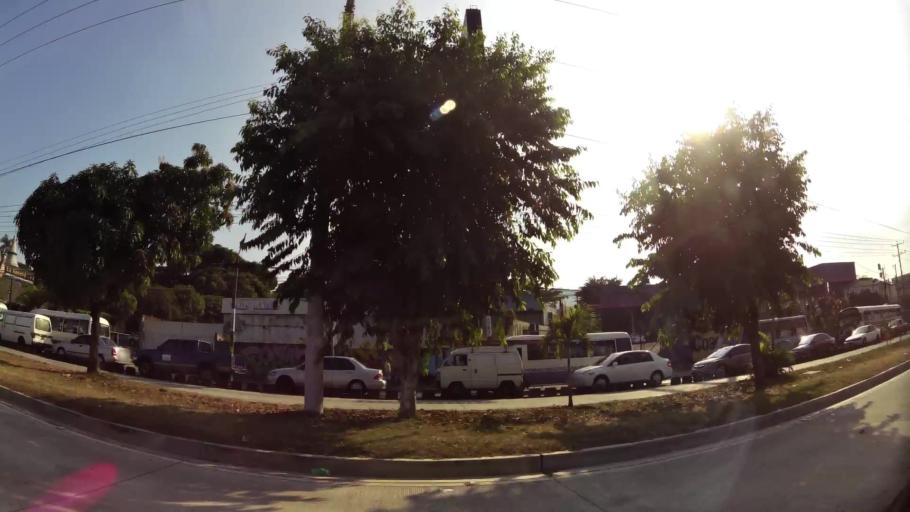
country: SV
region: San Salvador
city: Soyapango
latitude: 13.7006
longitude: -89.1540
